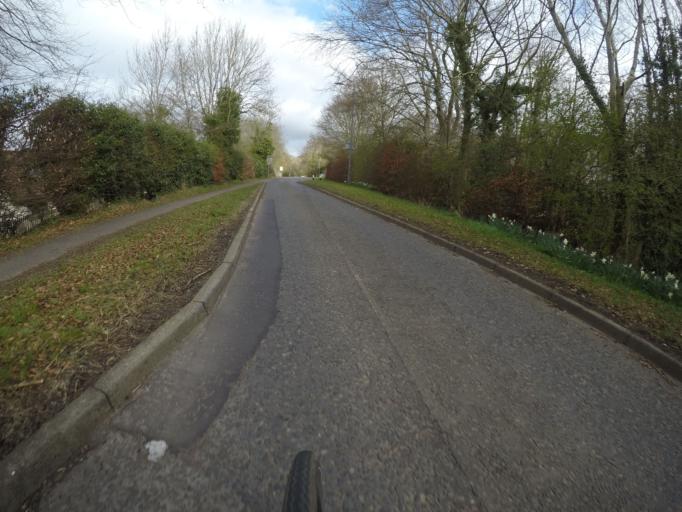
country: GB
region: Scotland
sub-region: North Ayrshire
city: Irvine
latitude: 55.6327
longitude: -4.6342
